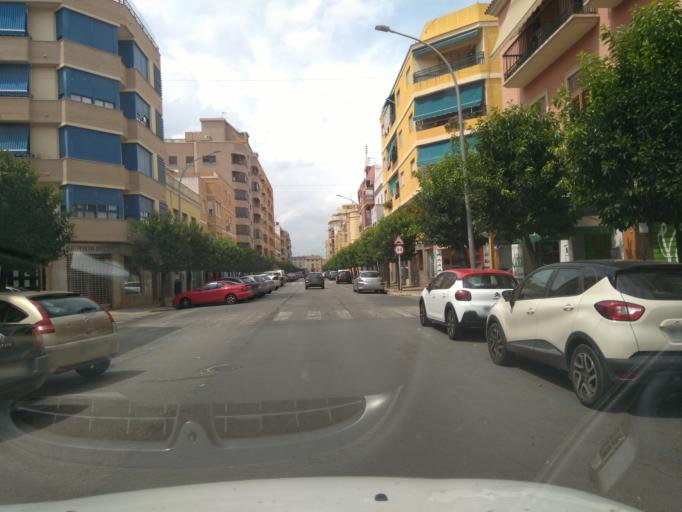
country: ES
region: Valencia
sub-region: Provincia de Valencia
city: Carcaixent
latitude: 39.1242
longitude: -0.4470
